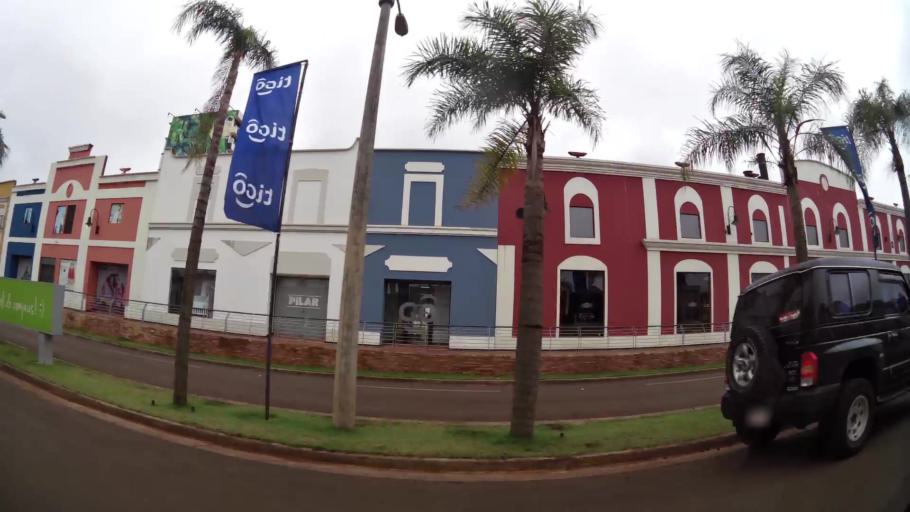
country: PY
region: Alto Parana
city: Ciudad del Este
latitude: -25.4973
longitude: -54.6795
